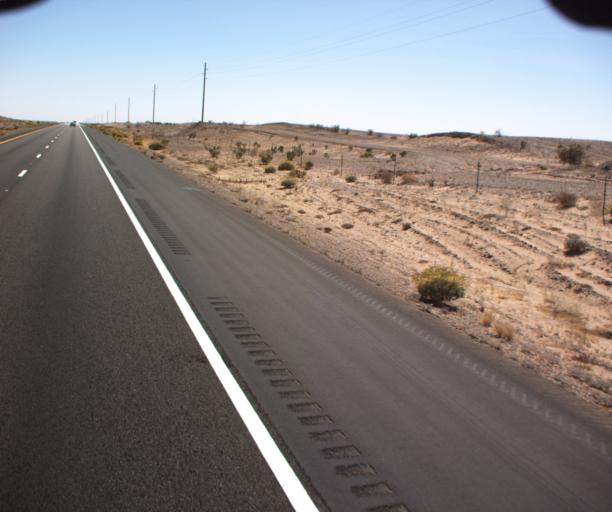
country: US
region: Arizona
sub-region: Yuma County
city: Somerton
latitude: 32.5407
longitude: -114.5623
